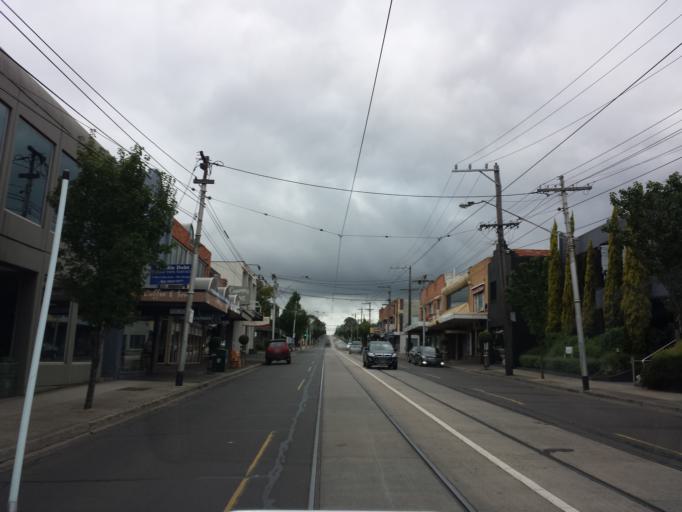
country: AU
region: Victoria
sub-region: Boroondara
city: Camberwell
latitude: -37.8486
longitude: 145.0798
